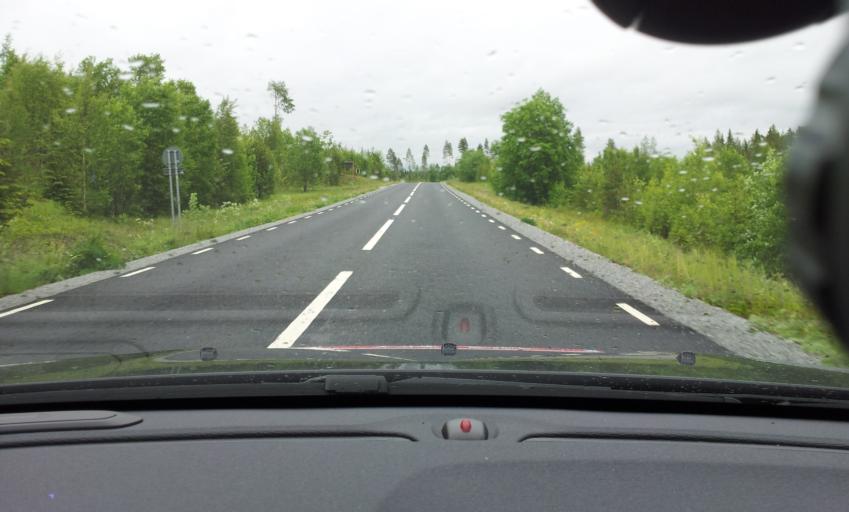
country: SE
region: Jaemtland
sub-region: OEstersunds Kommun
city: Lit
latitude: 63.7362
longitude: 14.8762
